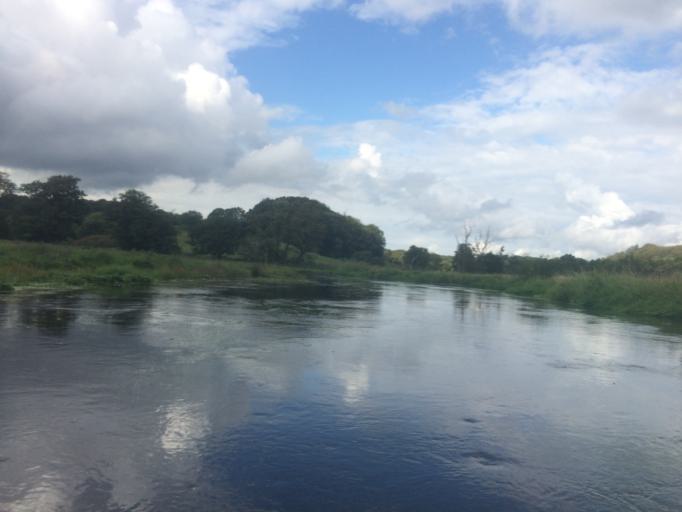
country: DK
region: South Denmark
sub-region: Vejle Kommune
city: Egtved
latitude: 55.6538
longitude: 9.3118
